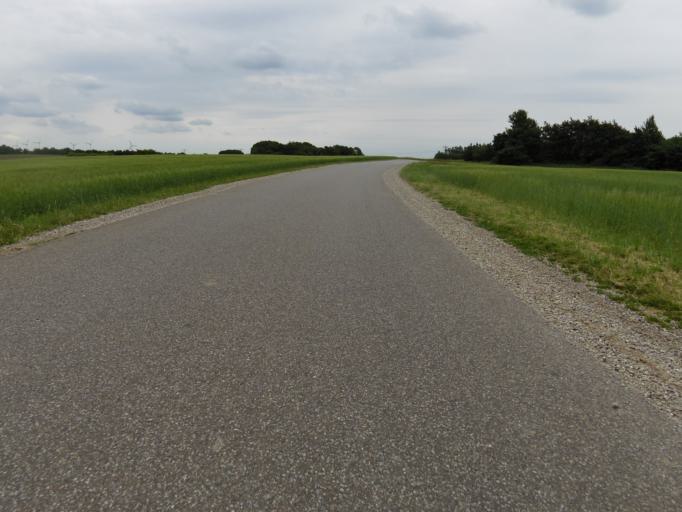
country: DK
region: Central Jutland
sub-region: Holstebro Kommune
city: Holstebro
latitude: 56.4064
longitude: 8.6730
